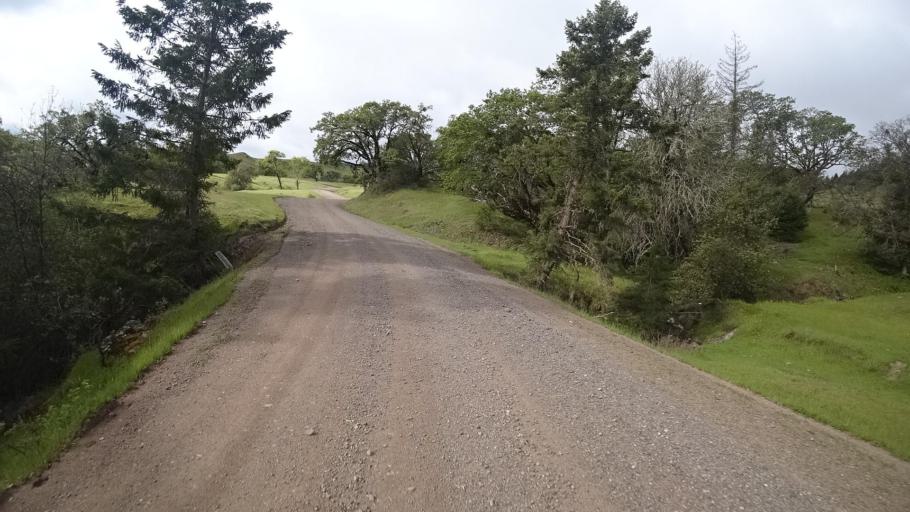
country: US
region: California
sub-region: Humboldt County
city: Redway
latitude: 40.2071
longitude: -123.6902
